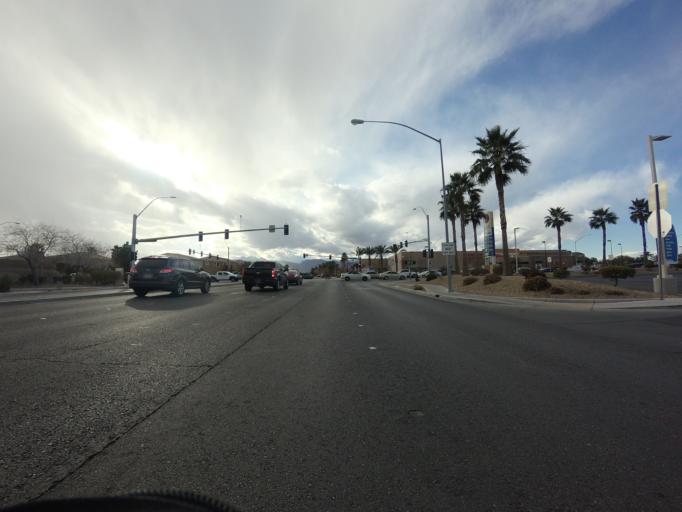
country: US
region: Nevada
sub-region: Clark County
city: North Las Vegas
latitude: 36.2691
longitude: -115.2062
